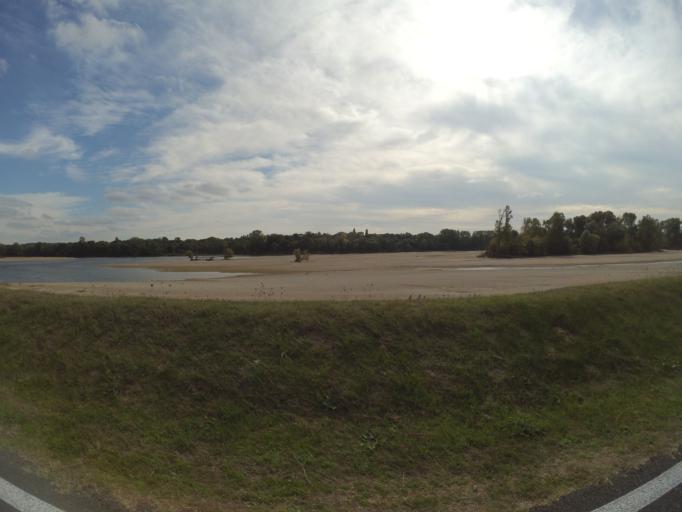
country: FR
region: Centre
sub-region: Departement d'Indre-et-Loire
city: La Chapelle-sur-Loire
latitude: 47.2465
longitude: 0.2160
